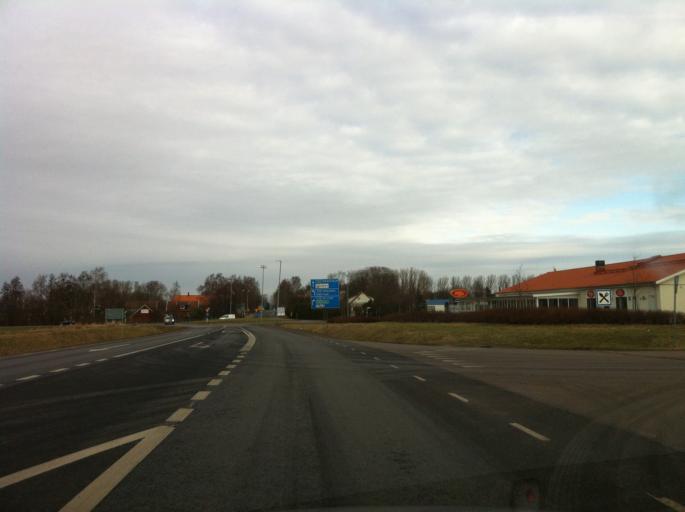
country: SE
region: Skane
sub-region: Angelholms Kommun
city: AEngelholm
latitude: 56.1926
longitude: 12.8504
